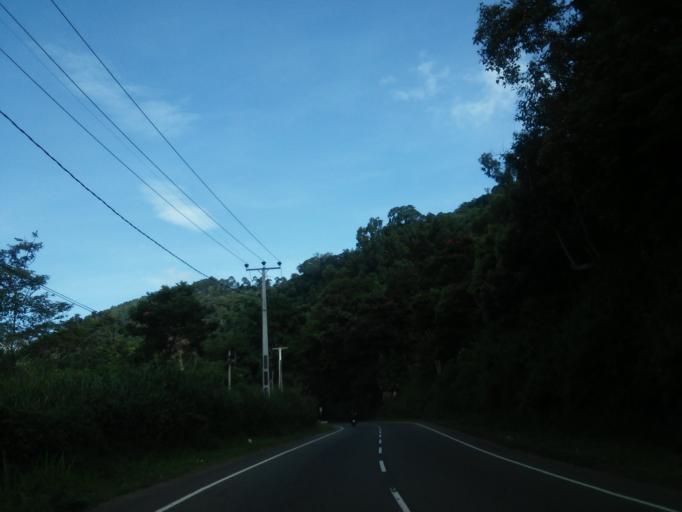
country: LK
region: Uva
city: Haputale
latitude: 6.7652
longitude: 80.8937
